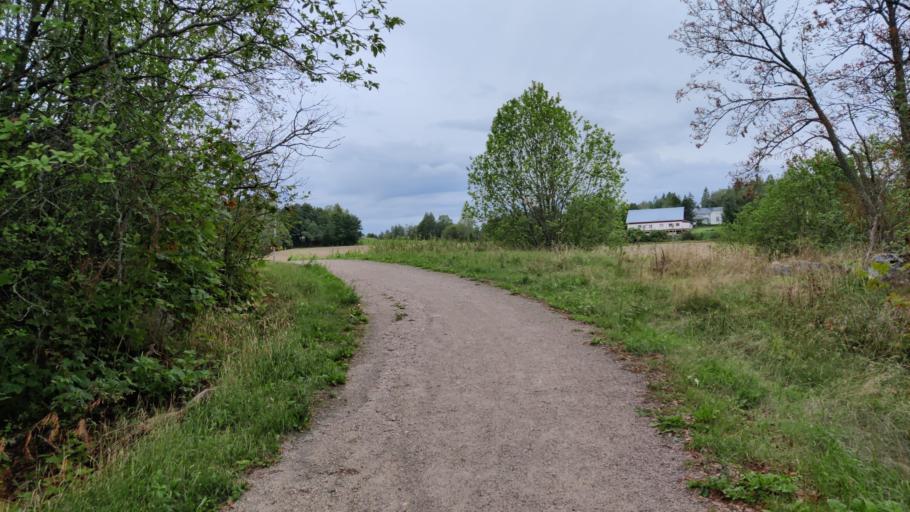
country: FI
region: Uusimaa
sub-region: Helsinki
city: Teekkarikylae
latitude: 60.2917
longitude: 24.8779
